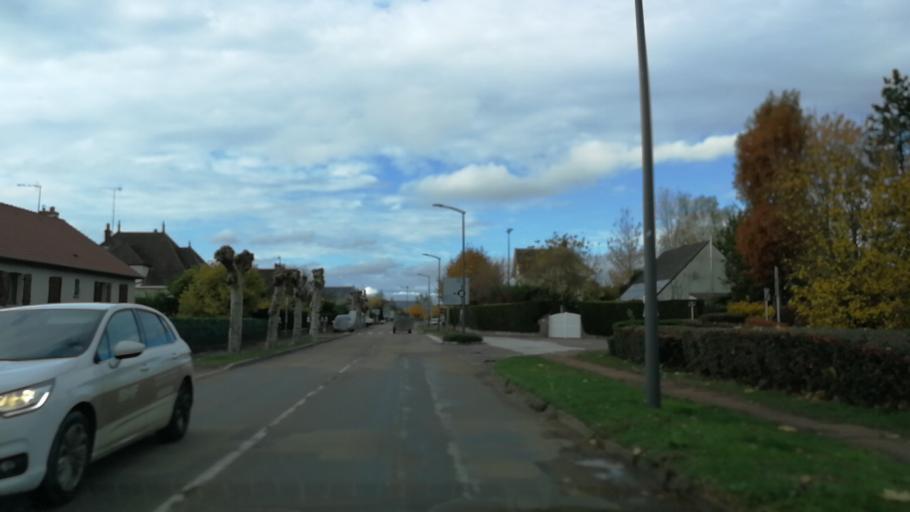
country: FR
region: Bourgogne
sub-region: Departement de la Cote-d'Or
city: Pouilly-en-Auxois
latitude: 47.2679
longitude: 4.5482
